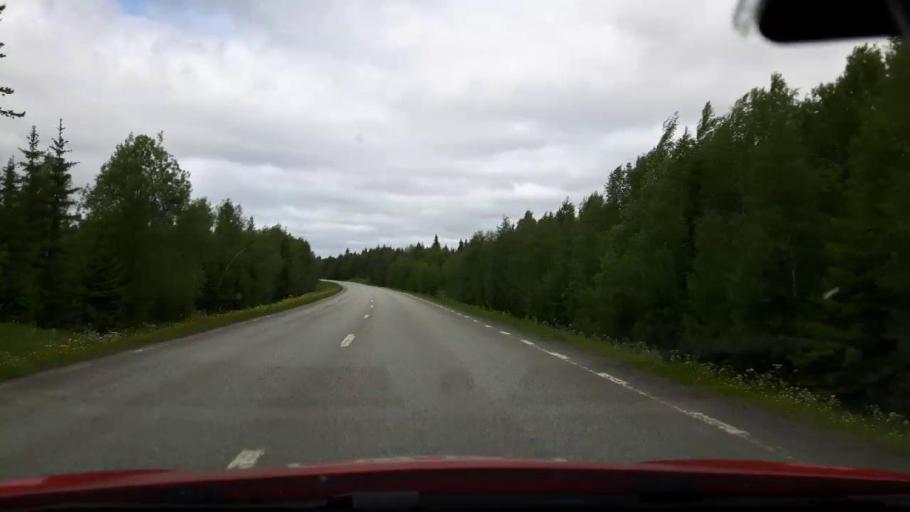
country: SE
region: Jaemtland
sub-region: Krokoms Kommun
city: Krokom
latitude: 63.3842
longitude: 14.5076
